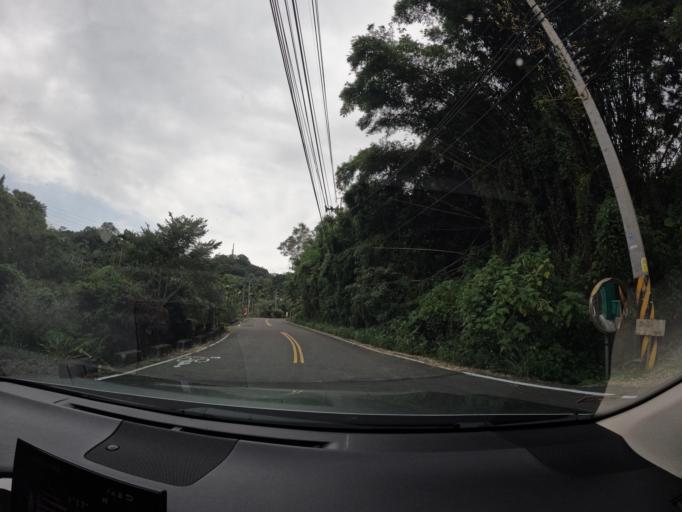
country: TW
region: Taiwan
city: Fengyuan
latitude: 24.3573
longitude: 120.8712
